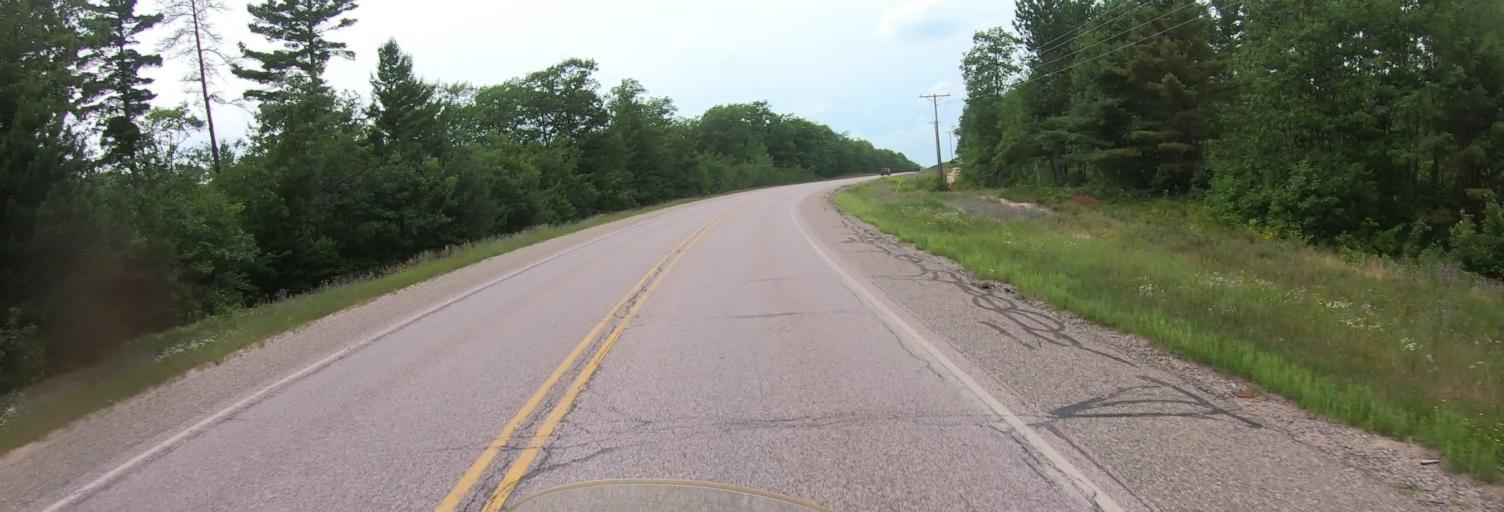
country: US
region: Michigan
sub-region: Marquette County
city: Harvey
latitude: 46.4586
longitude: -87.4102
